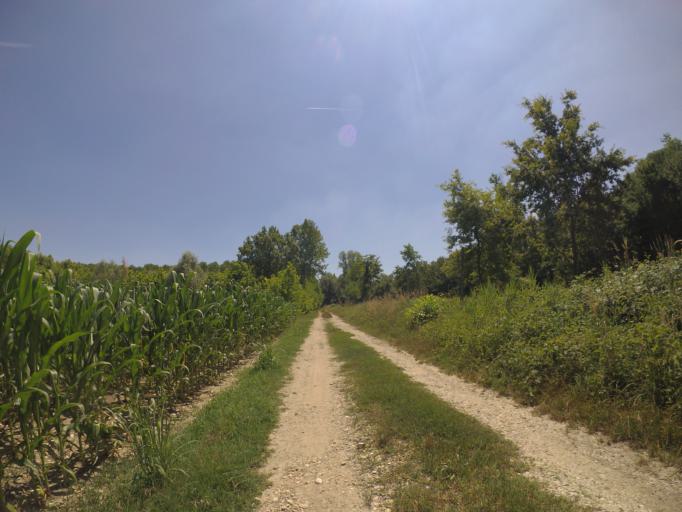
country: IT
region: Friuli Venezia Giulia
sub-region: Provincia di Udine
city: Rivignano
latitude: 45.9072
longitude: 13.0280
